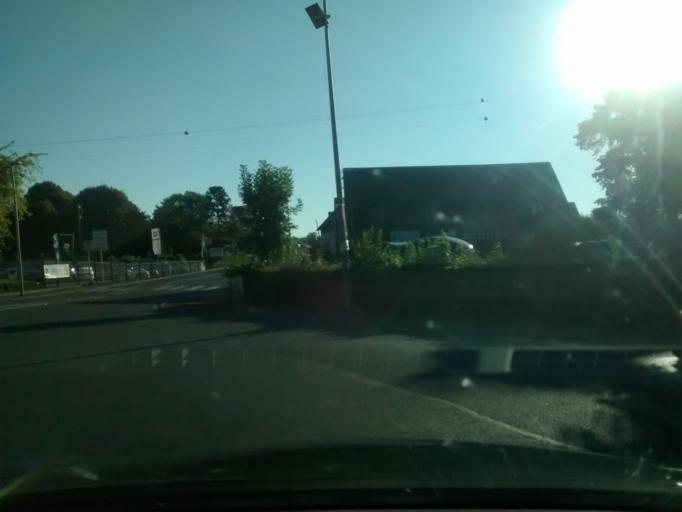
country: FR
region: Lower Normandy
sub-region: Departement du Calvados
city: Touques
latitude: 49.3389
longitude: 0.0990
